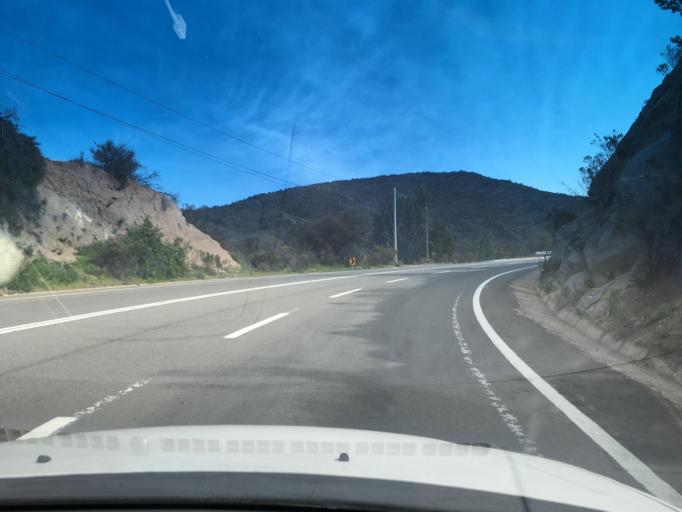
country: CL
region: Valparaiso
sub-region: Provincia de San Felipe
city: Llaillay
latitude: -33.0693
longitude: -70.9967
